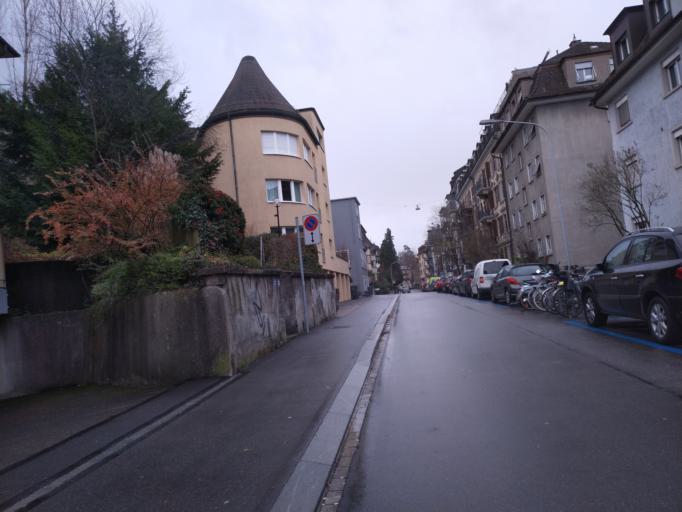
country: CH
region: Zurich
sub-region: Bezirk Zuerich
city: Zuerich (Kreis 2) / Enge
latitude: 47.3603
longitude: 8.5274
